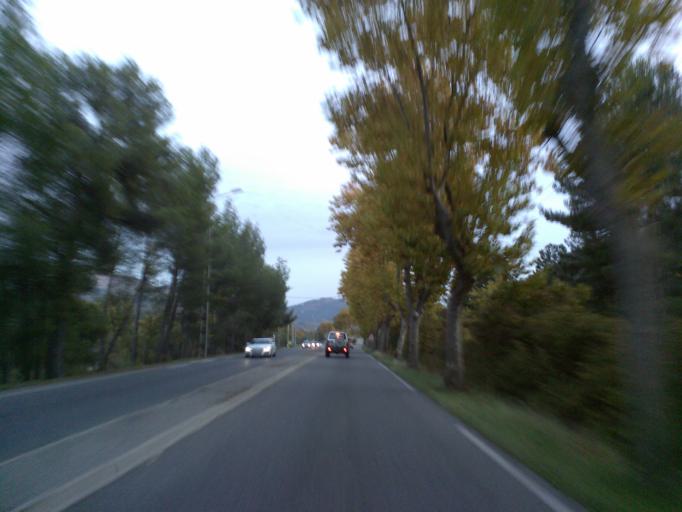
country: FR
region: Provence-Alpes-Cote d'Azur
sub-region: Departement des Alpes-de-Haute-Provence
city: Volonne
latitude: 44.1083
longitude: 6.0032
